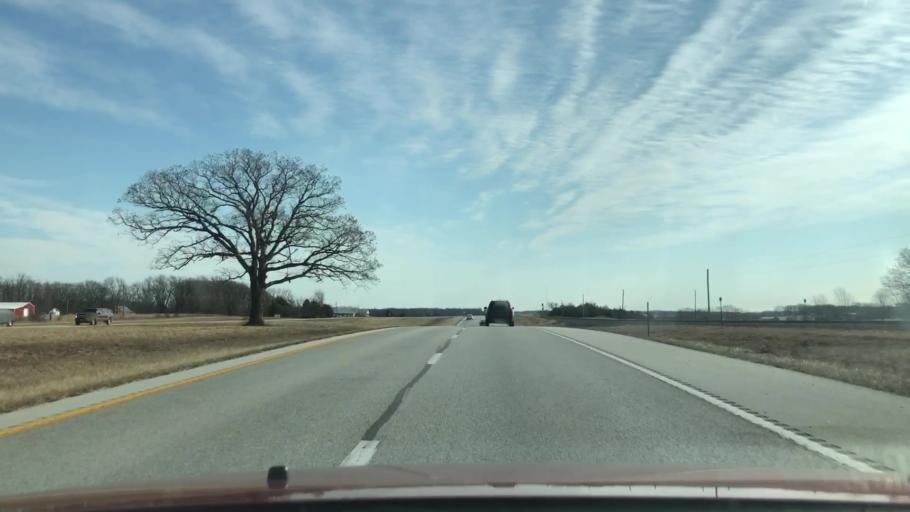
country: US
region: Missouri
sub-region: Webster County
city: Seymour
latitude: 37.1292
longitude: -92.7160
